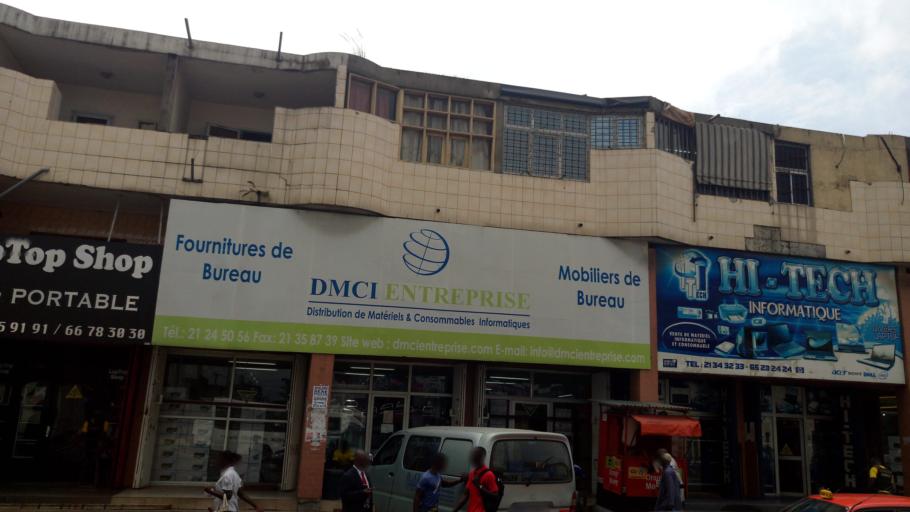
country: CI
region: Lagunes
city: Abidjan
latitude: 5.3099
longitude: -4.0061
